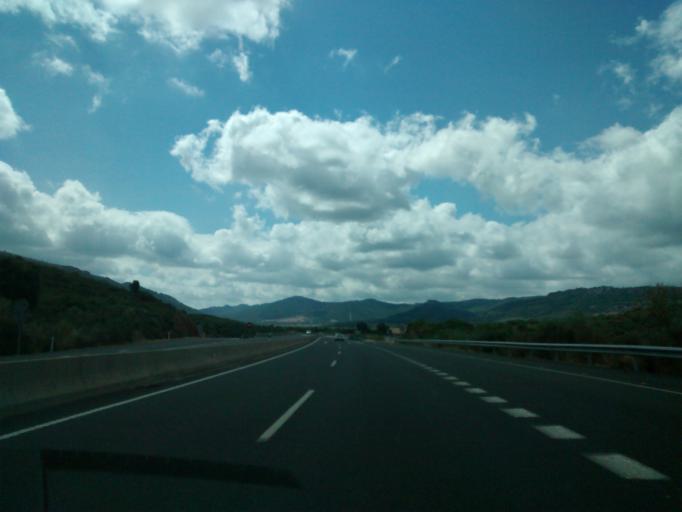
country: ES
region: Extremadura
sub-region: Provincia de Caceres
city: Casas de Miravete
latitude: 39.7342
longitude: -5.7222
